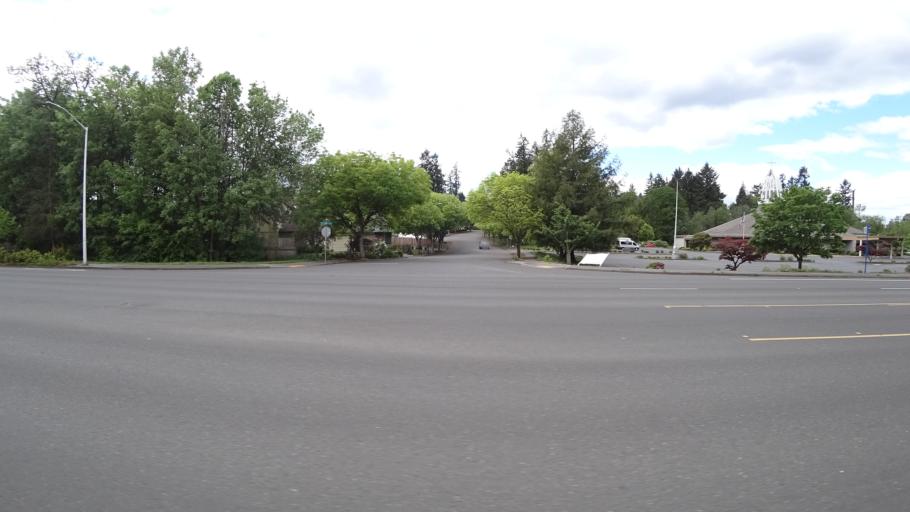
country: US
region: Oregon
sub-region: Washington County
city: Beaverton
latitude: 45.4721
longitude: -122.8051
